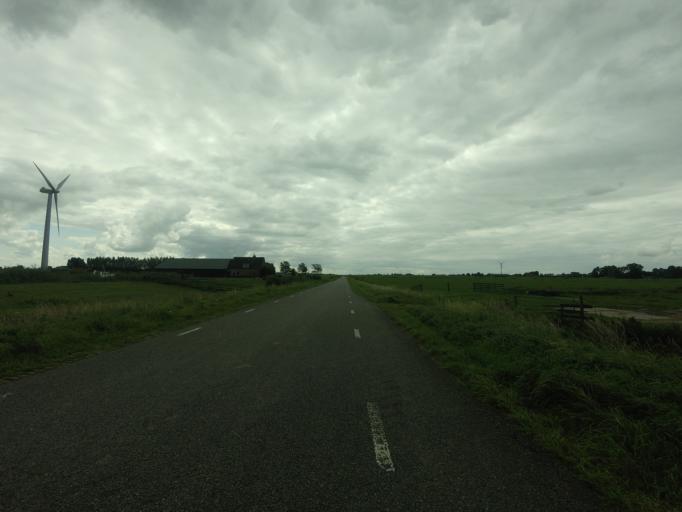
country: NL
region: Friesland
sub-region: Sudwest Fryslan
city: IJlst
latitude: 53.0032
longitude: 5.6350
